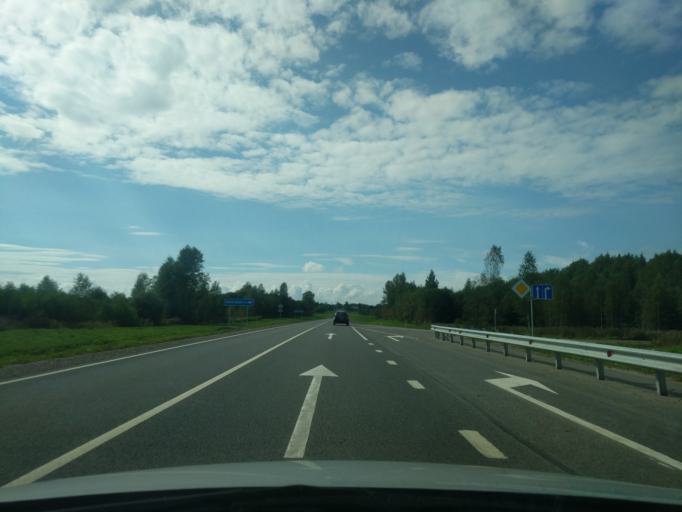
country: RU
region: Kostroma
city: Oktyabr'skiy
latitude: 57.7979
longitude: 41.2246
